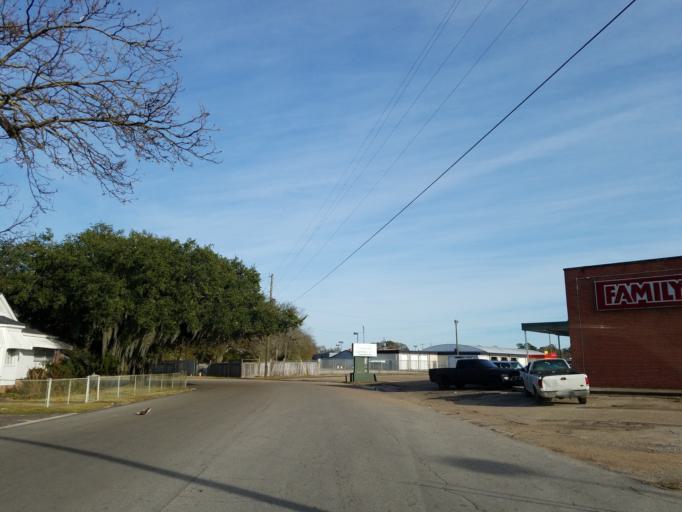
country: US
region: Mississippi
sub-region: Forrest County
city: Hattiesburg
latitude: 31.3174
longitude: -89.3062
